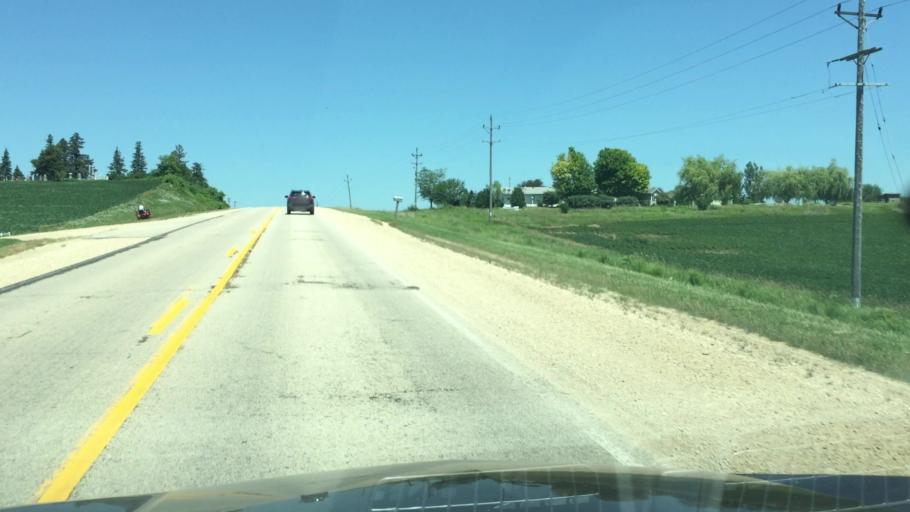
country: US
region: Iowa
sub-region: Cedar County
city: Mechanicsville
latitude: 41.9811
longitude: -91.1416
